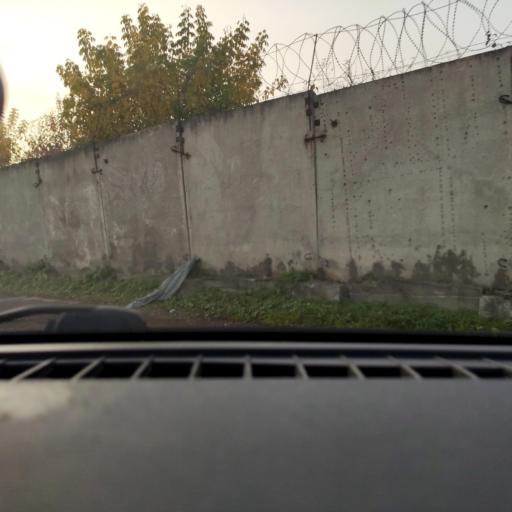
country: RU
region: Perm
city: Kondratovo
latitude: 58.0112
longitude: 56.1624
